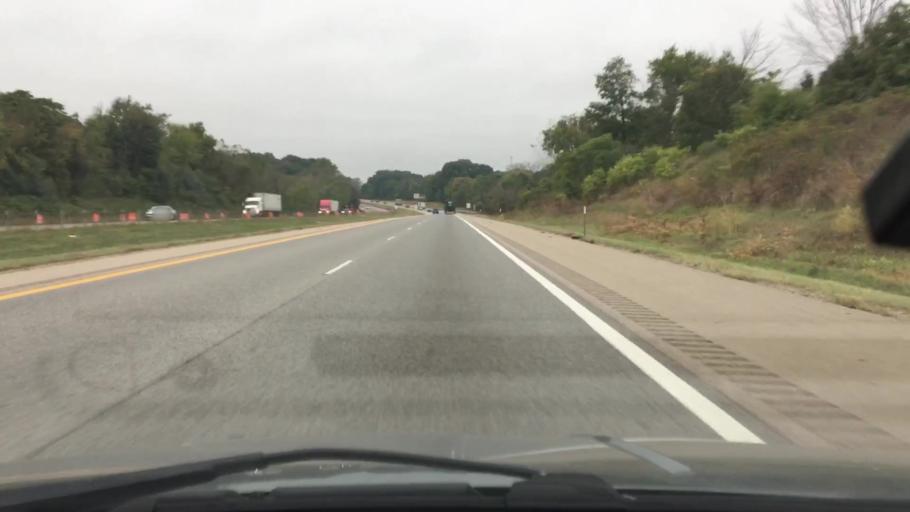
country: US
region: Michigan
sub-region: Van Buren County
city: Hartford
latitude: 42.1975
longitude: -86.0925
